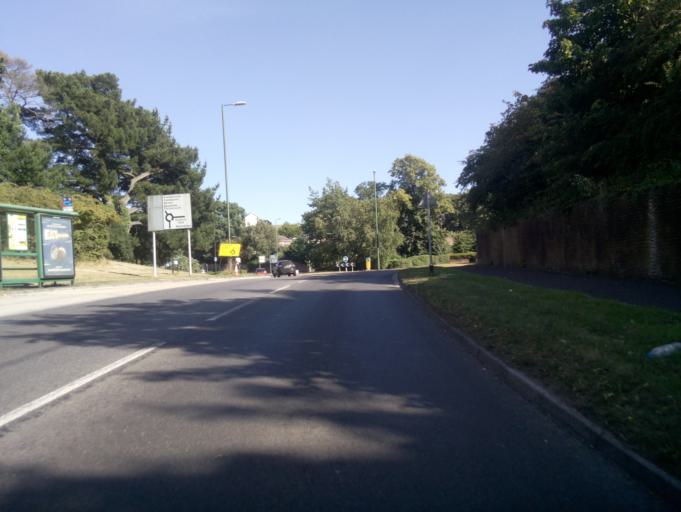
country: GB
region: England
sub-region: Bournemouth
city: Bournemouth
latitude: 50.7623
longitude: -1.8755
